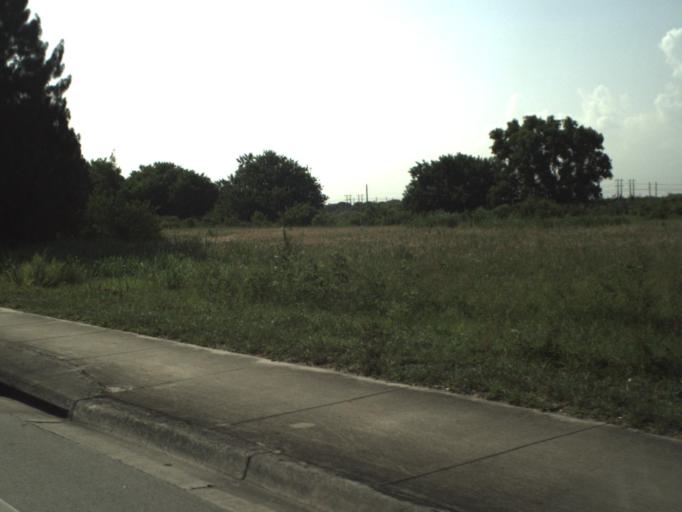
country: US
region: Florida
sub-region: Broward County
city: Coconut Creek
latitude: 26.2741
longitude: -80.1899
